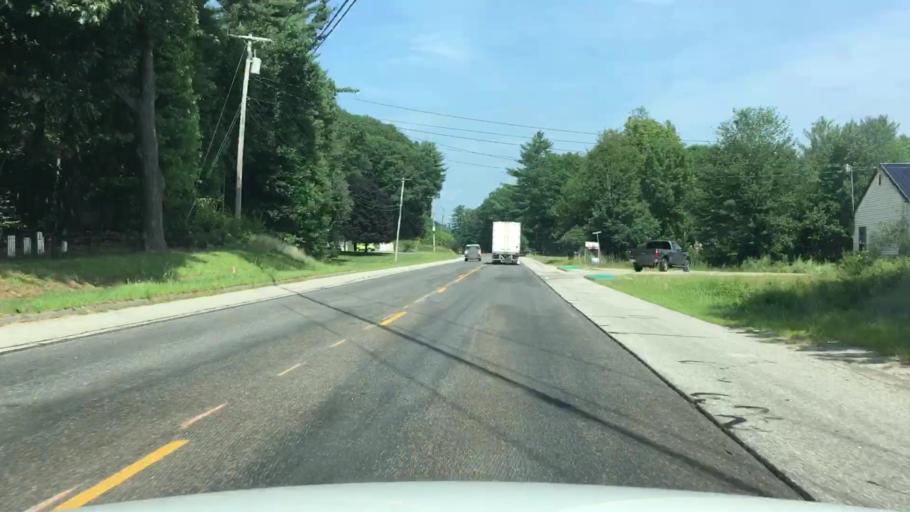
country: US
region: Maine
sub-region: Androscoggin County
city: Turner
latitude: 44.3059
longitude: -70.2667
